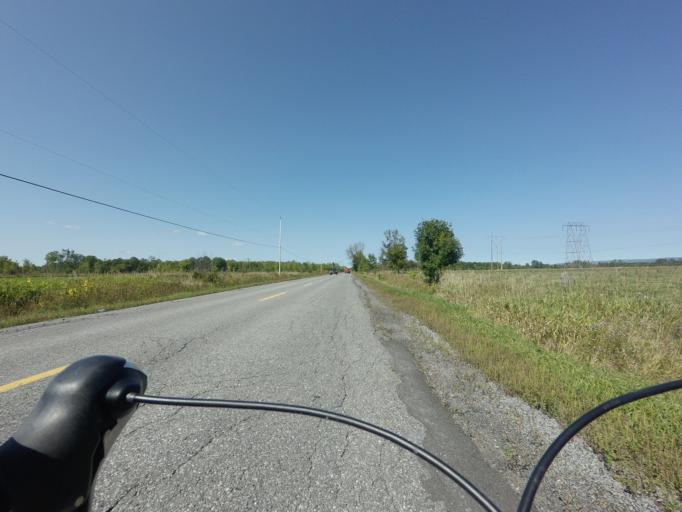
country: CA
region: Ontario
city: Bells Corners
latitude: 45.3796
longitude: -76.0132
